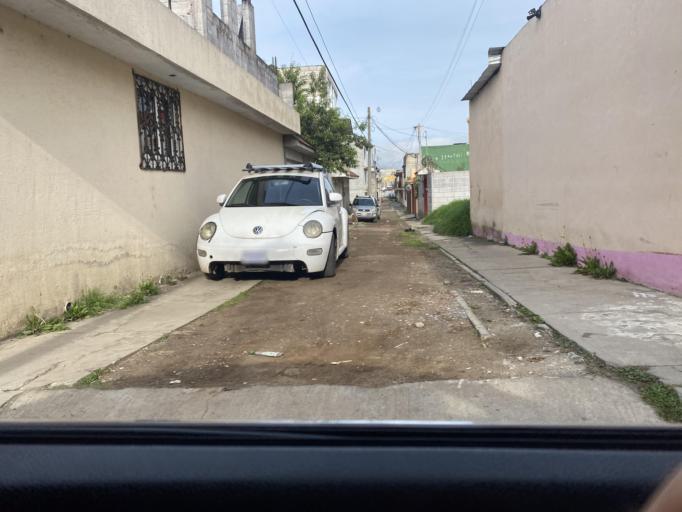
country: GT
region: Quetzaltenango
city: Olintepeque
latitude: 14.8599
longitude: -91.5188
